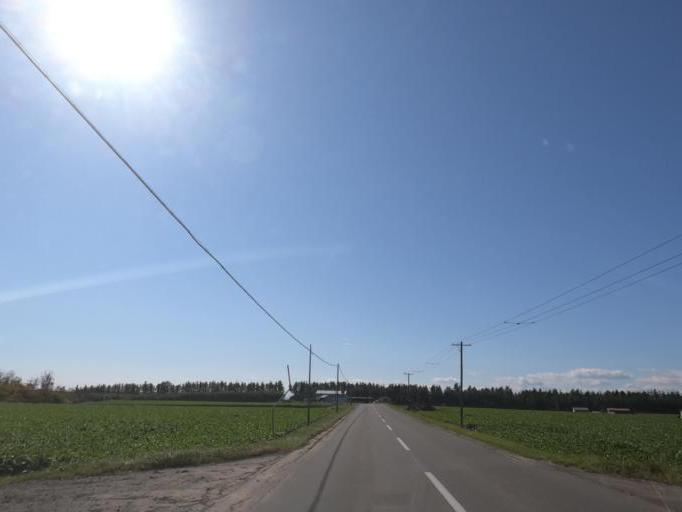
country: JP
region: Hokkaido
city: Obihiro
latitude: 42.8176
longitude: 143.2556
